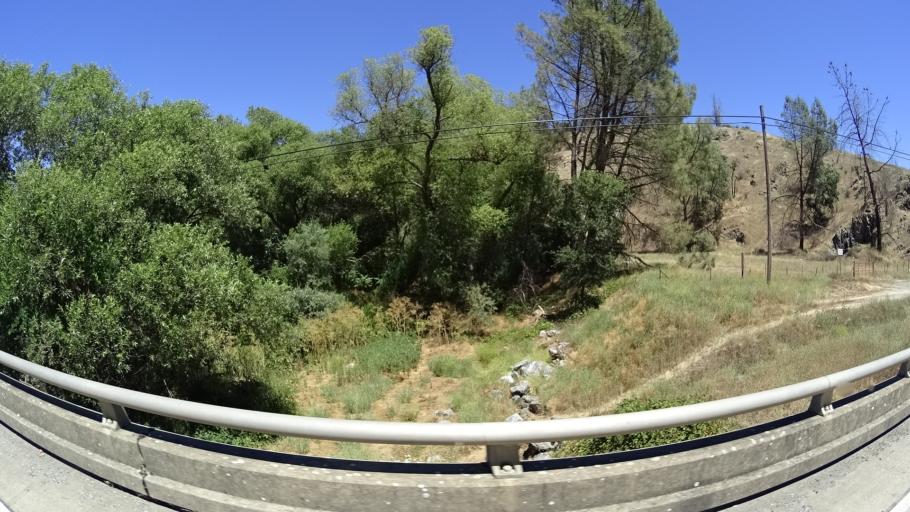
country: US
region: California
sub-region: Calaveras County
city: San Andreas
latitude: 38.2186
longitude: -120.6987
